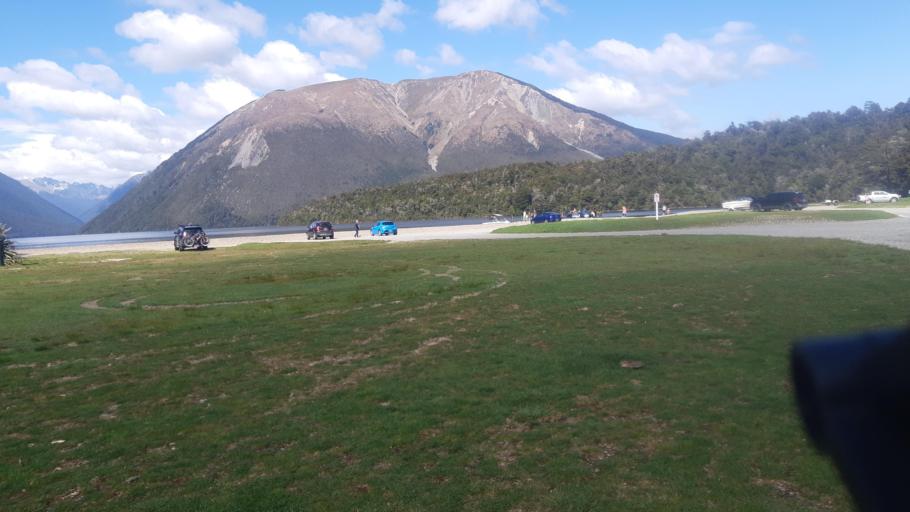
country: NZ
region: Tasman
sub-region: Tasman District
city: Wakefield
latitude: -41.8061
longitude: 172.8462
